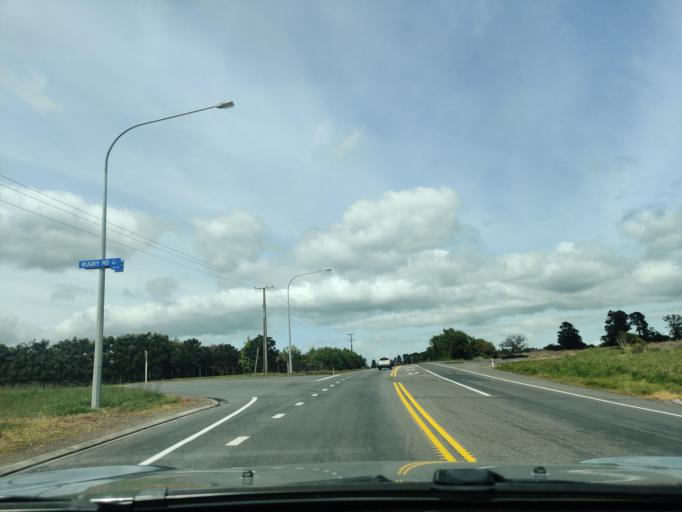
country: NZ
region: Taranaki
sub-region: New Plymouth District
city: New Plymouth
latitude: -39.2170
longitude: 174.2367
